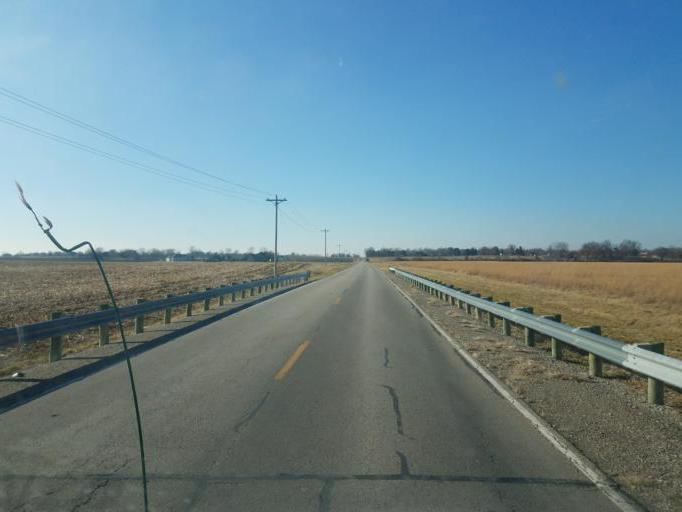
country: US
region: Ohio
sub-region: Marion County
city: Marion
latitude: 40.6444
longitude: -83.1625
